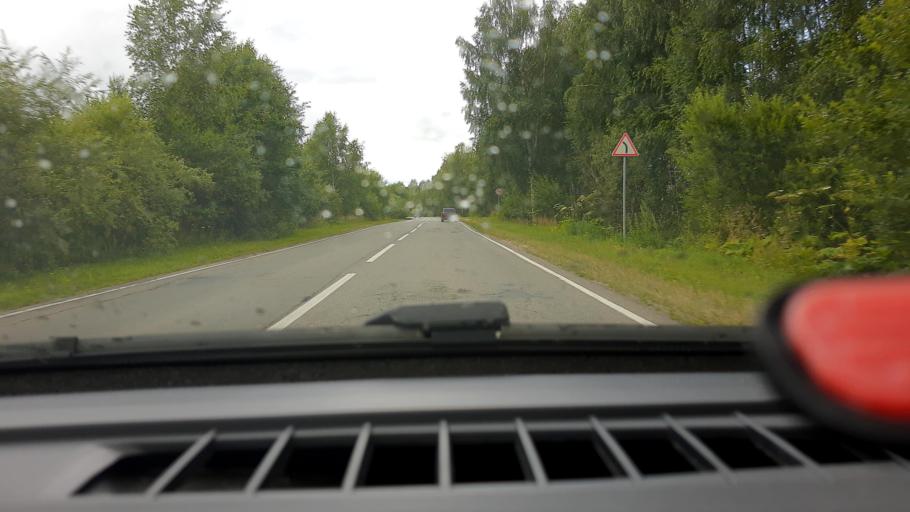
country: RU
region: Nizjnij Novgorod
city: Neklyudovo
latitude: 56.5277
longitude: 43.8399
